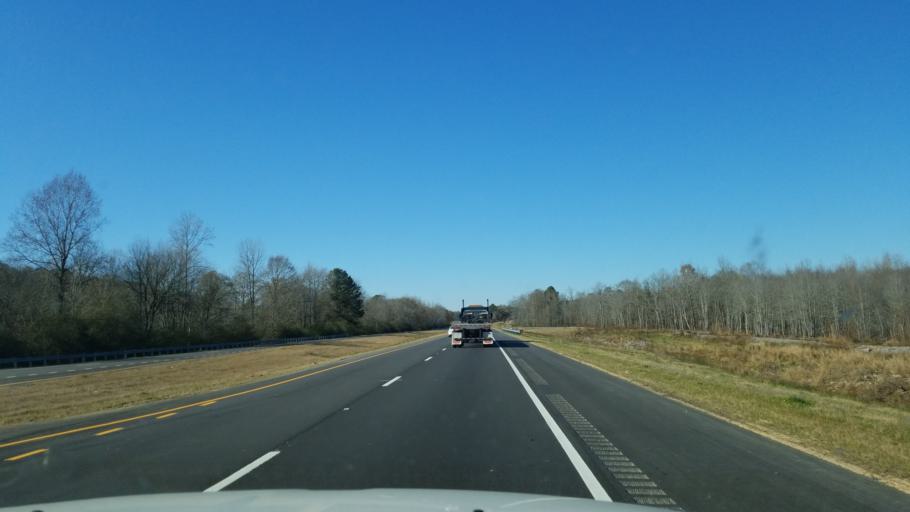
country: US
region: Alabama
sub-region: Pickens County
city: Gordo
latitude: 33.3451
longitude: -87.9471
